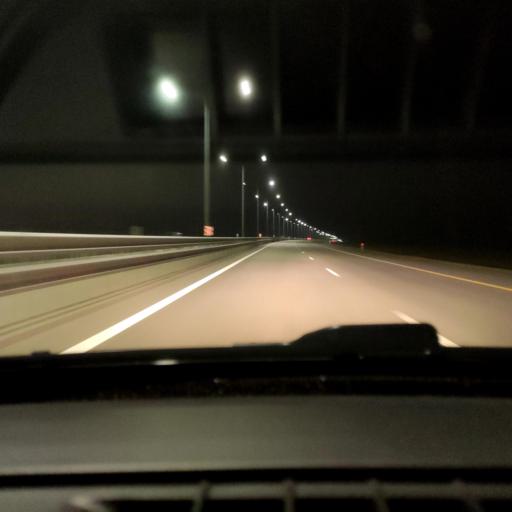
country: RU
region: Voronezj
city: Podkletnoye
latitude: 51.5789
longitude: 39.4639
